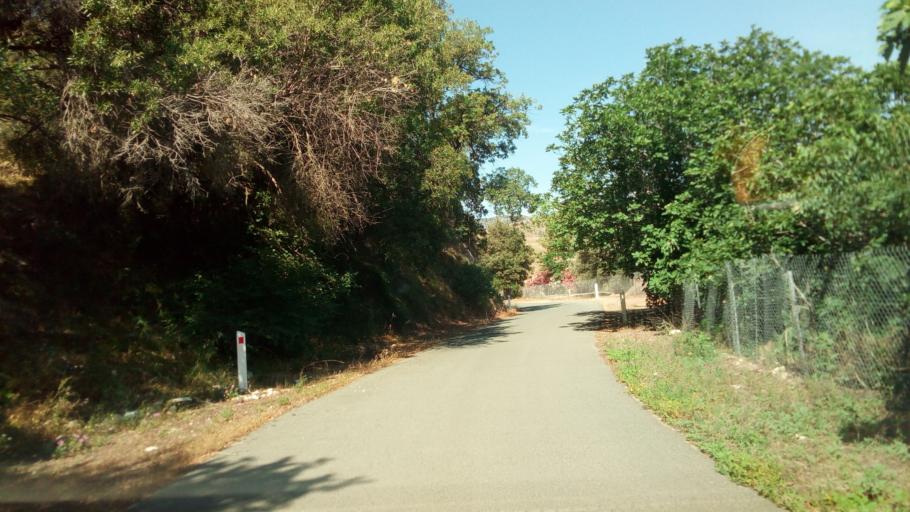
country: CY
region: Limassol
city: Pachna
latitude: 34.8145
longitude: 32.7219
